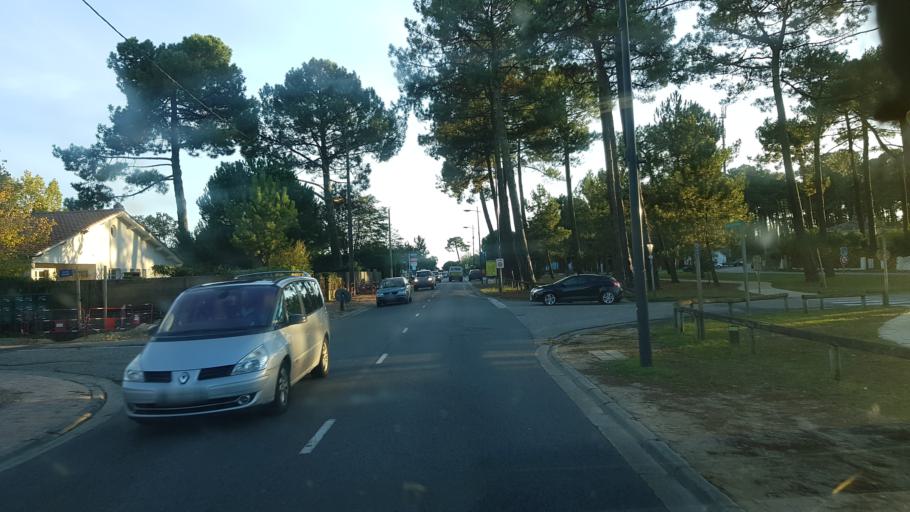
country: FR
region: Aquitaine
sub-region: Departement de la Gironde
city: Ares
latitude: 44.7483
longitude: -1.1810
